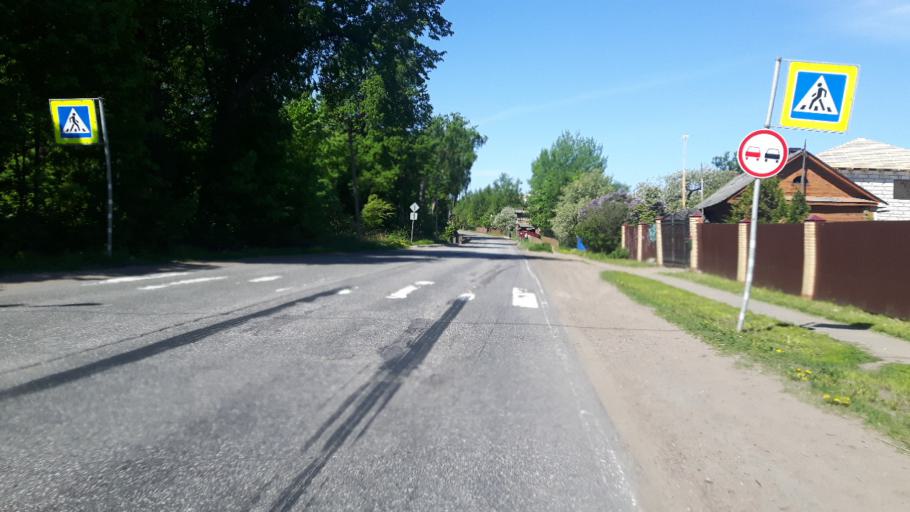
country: RU
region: Leningrad
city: Lebyazh'ye
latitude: 59.9607
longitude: 29.4264
